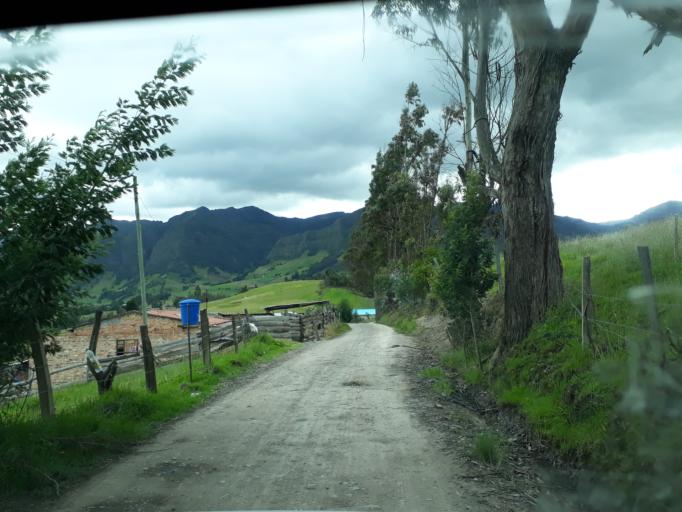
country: CO
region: Cundinamarca
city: La Mesa
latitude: 5.2737
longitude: -73.9013
